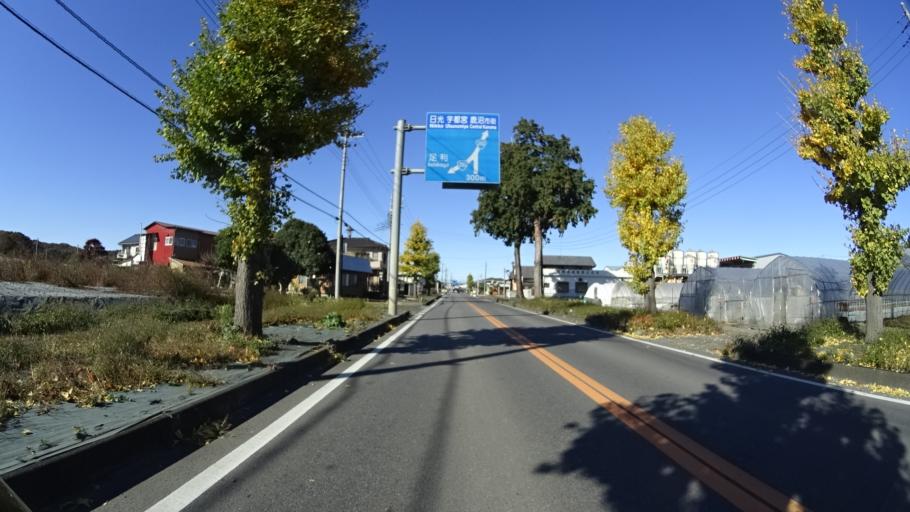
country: JP
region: Tochigi
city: Kanuma
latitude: 36.5005
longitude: 139.7524
